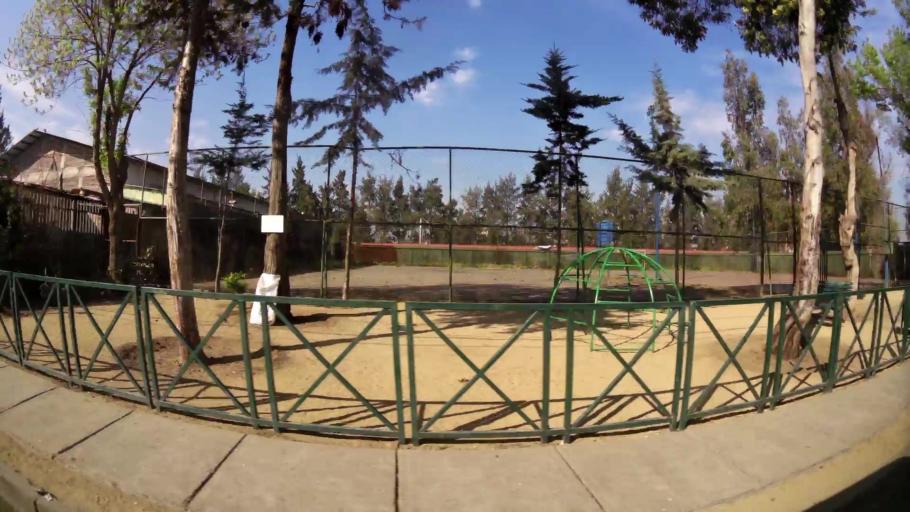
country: CL
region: Santiago Metropolitan
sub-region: Provincia de Santiago
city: Lo Prado
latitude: -33.4640
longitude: -70.7580
